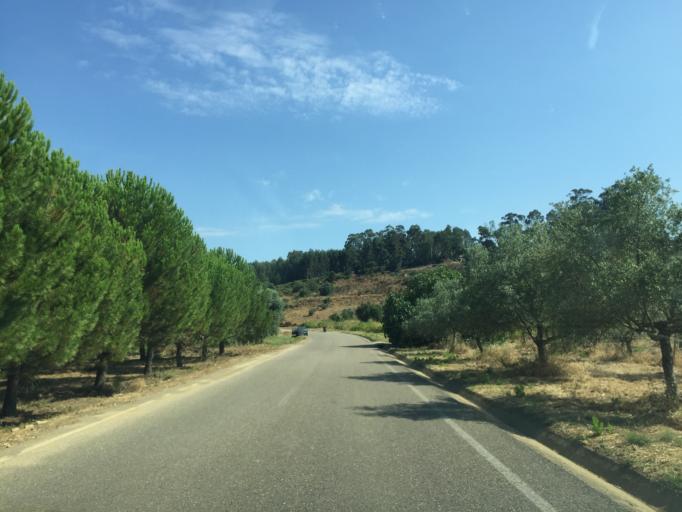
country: PT
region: Santarem
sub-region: Ferreira do Zezere
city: Ferreira do Zezere
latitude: 39.5930
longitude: -8.2984
